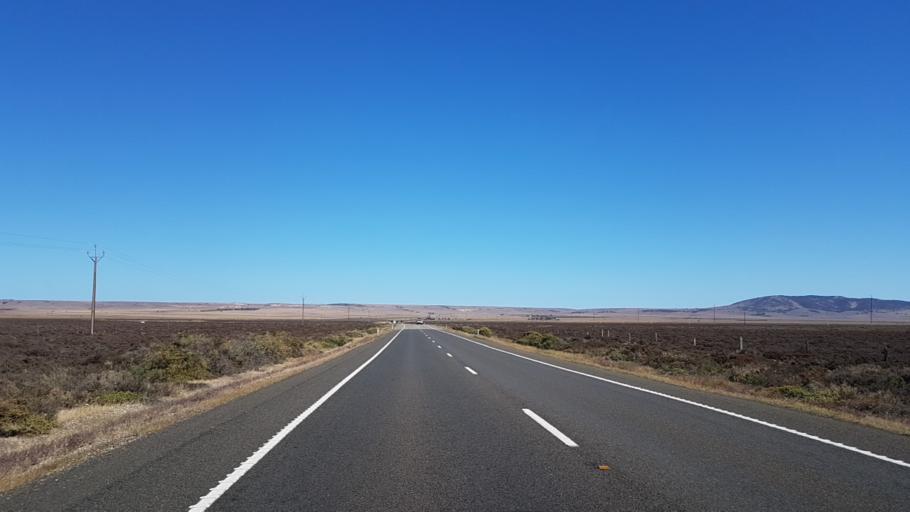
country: AU
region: South Australia
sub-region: Wakefield
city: Balaklava
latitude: -34.1042
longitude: 138.1114
